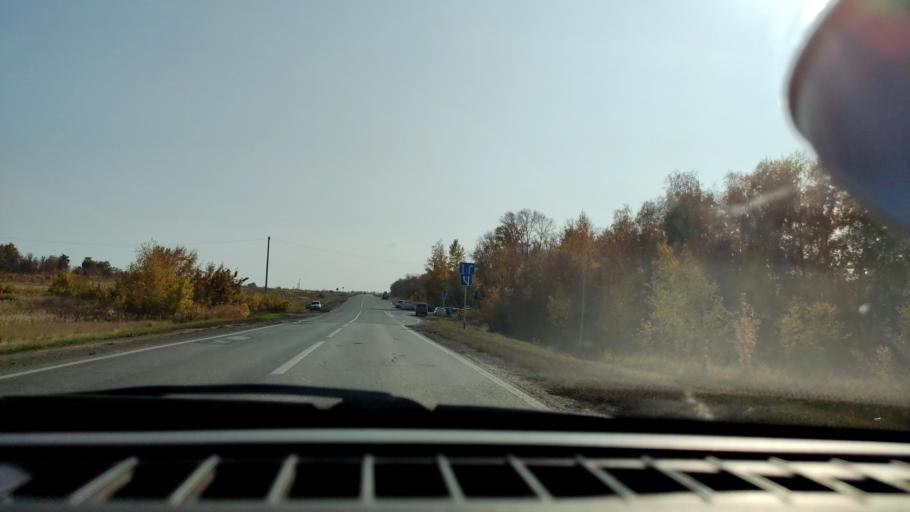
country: RU
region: Samara
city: Dubovyy Umet
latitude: 53.0952
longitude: 50.3496
